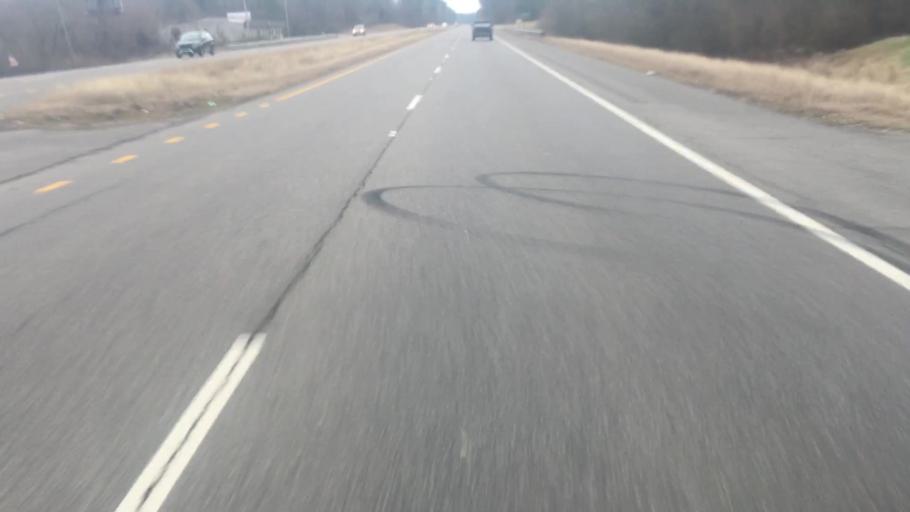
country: US
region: Alabama
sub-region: Walker County
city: Jasper
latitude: 33.8301
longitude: -87.2087
